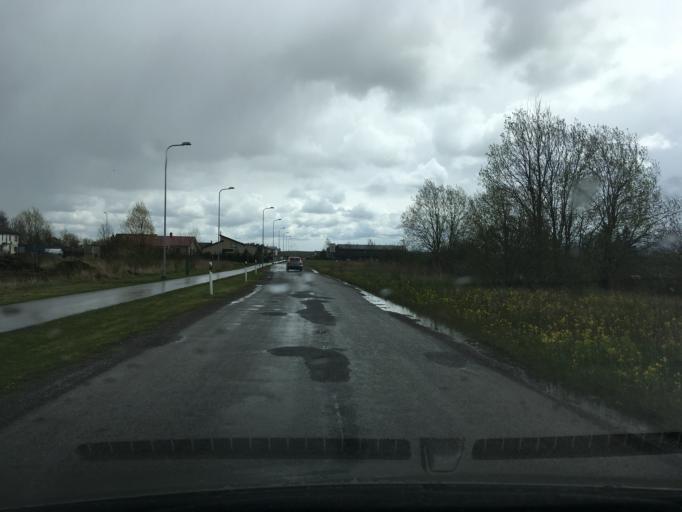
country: EE
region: Harju
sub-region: Joelaehtme vald
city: Loo
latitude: 59.4450
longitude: 24.9591
